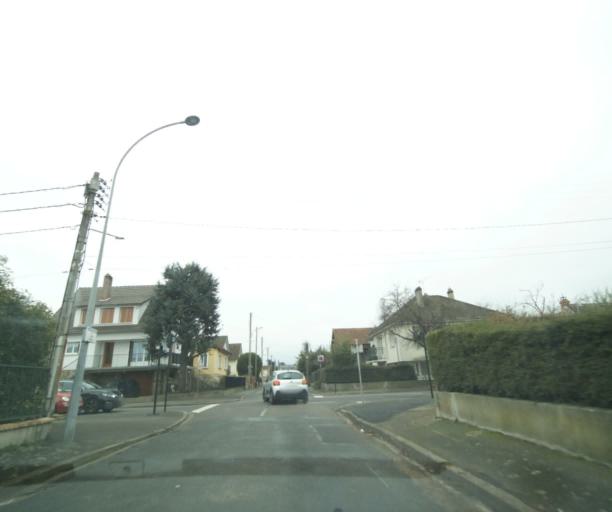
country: FR
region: Ile-de-France
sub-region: Departement du Val-de-Marne
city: Ablon-sur-Seine
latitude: 48.7268
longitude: 2.4283
